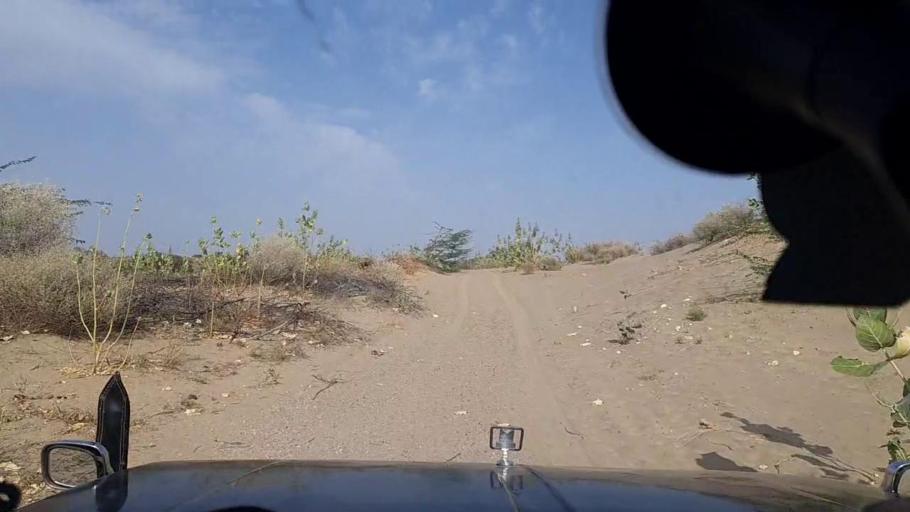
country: PK
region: Sindh
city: Diplo
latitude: 24.4510
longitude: 69.4691
